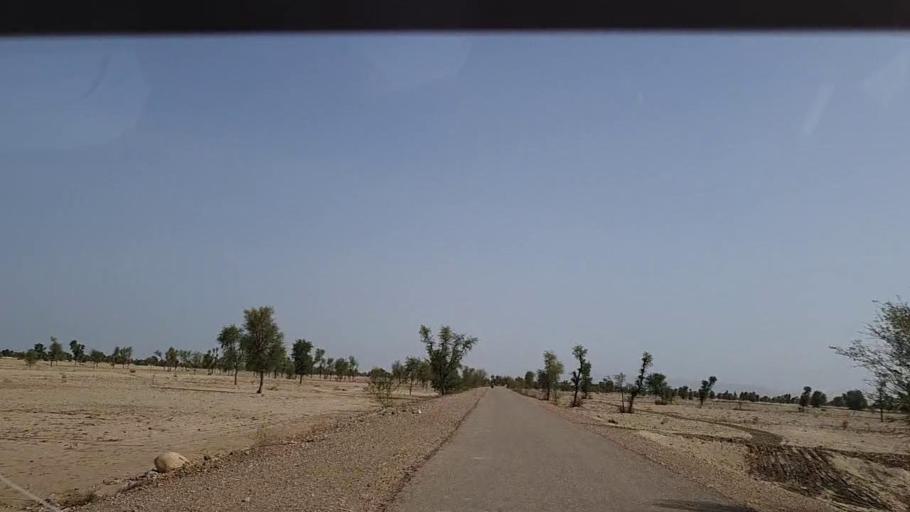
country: PK
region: Sindh
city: Johi
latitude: 26.6304
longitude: 67.5010
